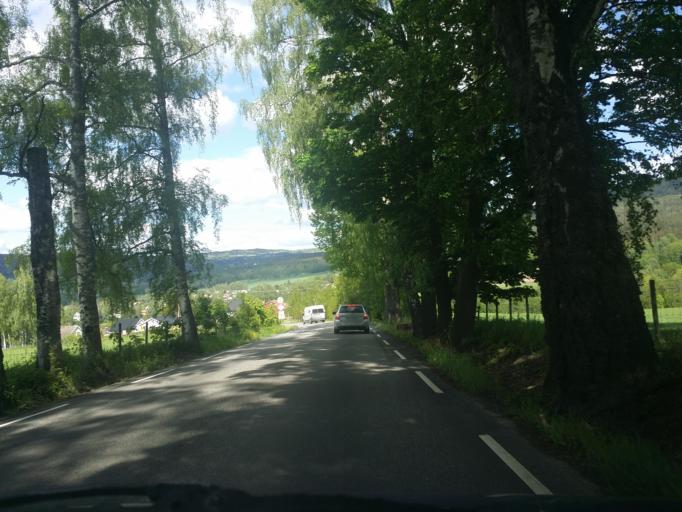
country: NO
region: Oppland
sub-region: Jevnaker
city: Jevnaker
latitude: 60.2348
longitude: 10.4054
